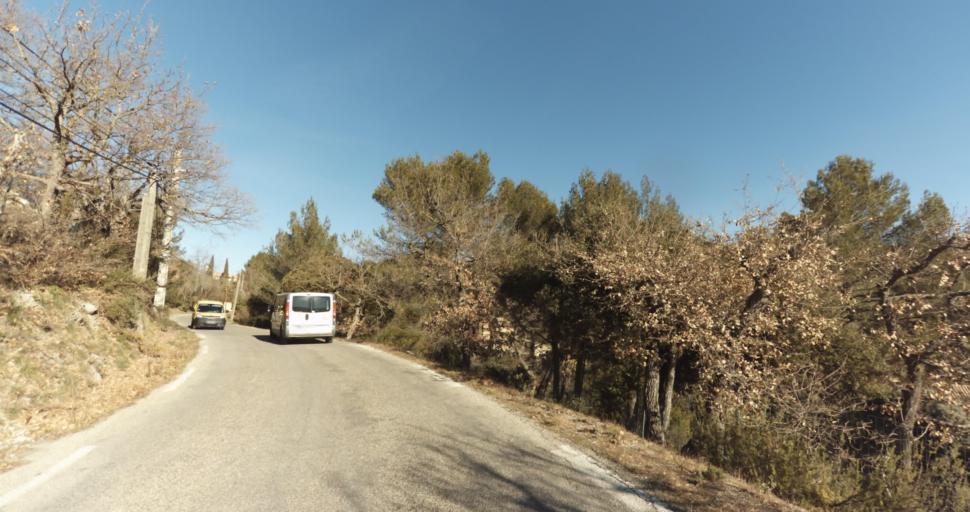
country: FR
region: Provence-Alpes-Cote d'Azur
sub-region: Departement des Bouches-du-Rhone
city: Peypin
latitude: 43.3768
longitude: 5.5665
